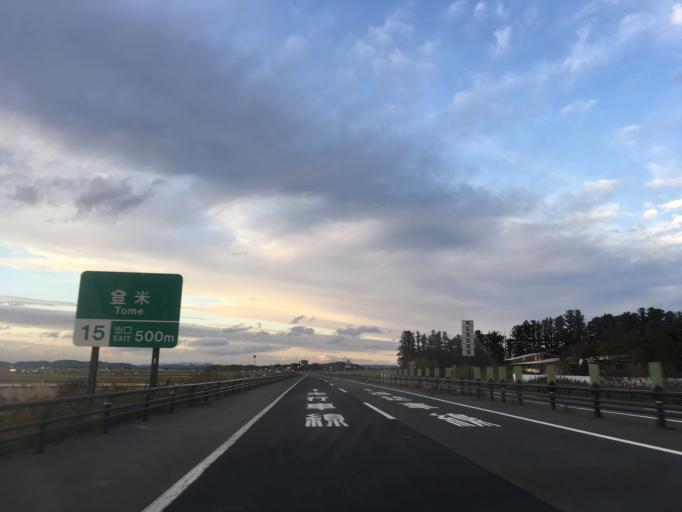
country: JP
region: Miyagi
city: Wakuya
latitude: 38.6694
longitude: 141.2655
